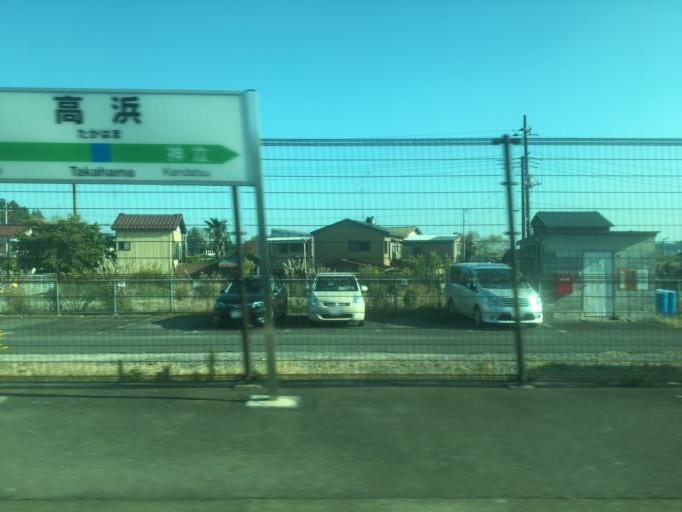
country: JP
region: Ibaraki
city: Ishioka
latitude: 36.1632
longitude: 140.2945
